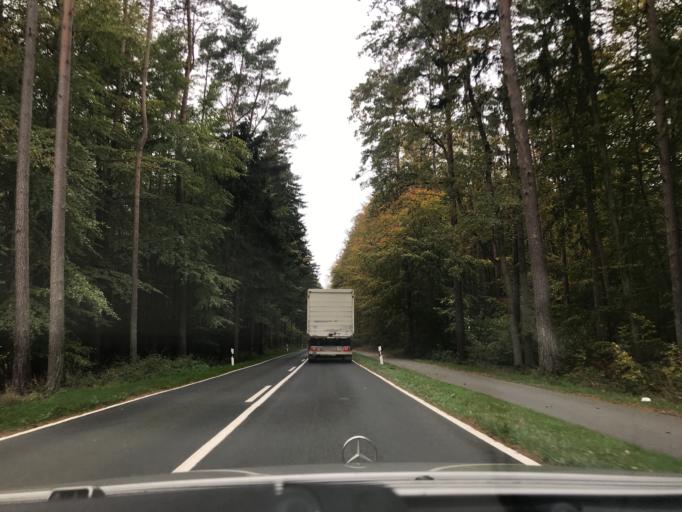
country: DE
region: Mecklenburg-Vorpommern
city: Kroslin
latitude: 54.1393
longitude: 13.7063
